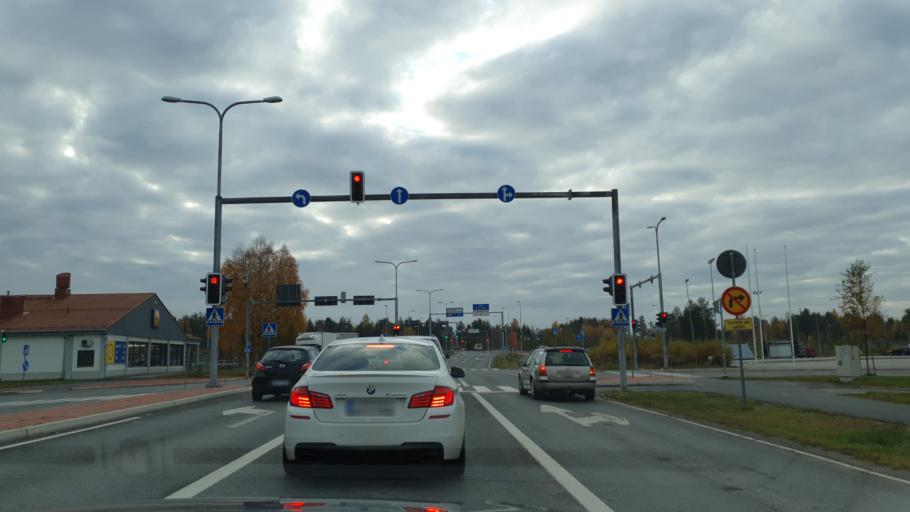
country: FI
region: Lapland
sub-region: Rovaniemi
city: Rovaniemi
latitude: 66.4921
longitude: 25.6921
